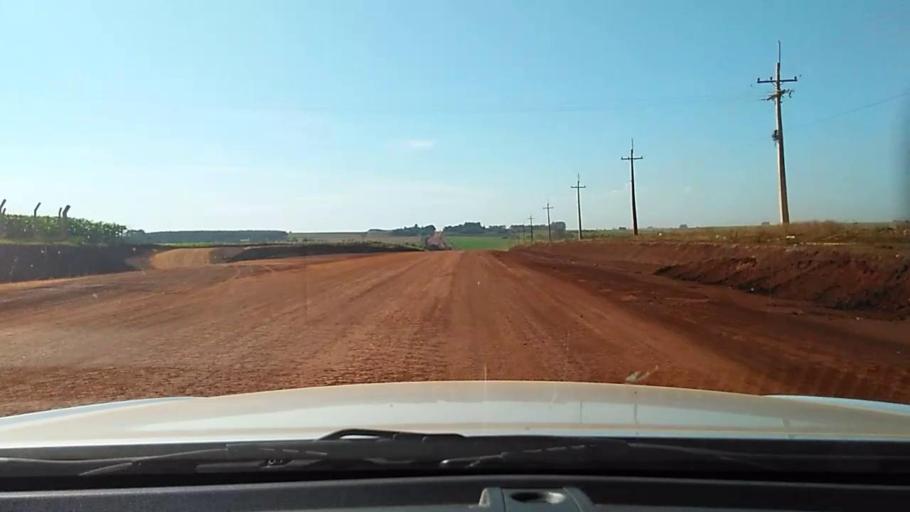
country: PY
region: Alto Parana
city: Naranjal
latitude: -25.9220
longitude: -55.4128
